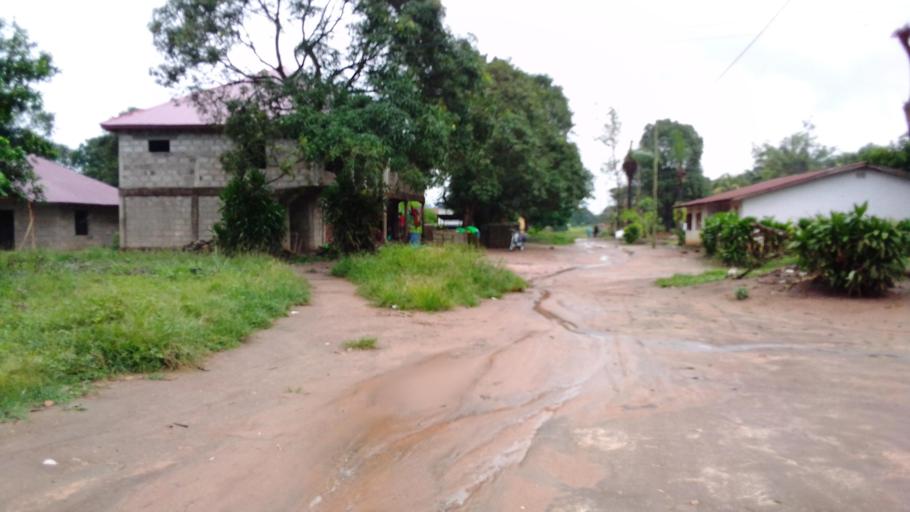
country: SL
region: Eastern Province
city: Kenema
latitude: 7.8949
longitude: -11.1735
